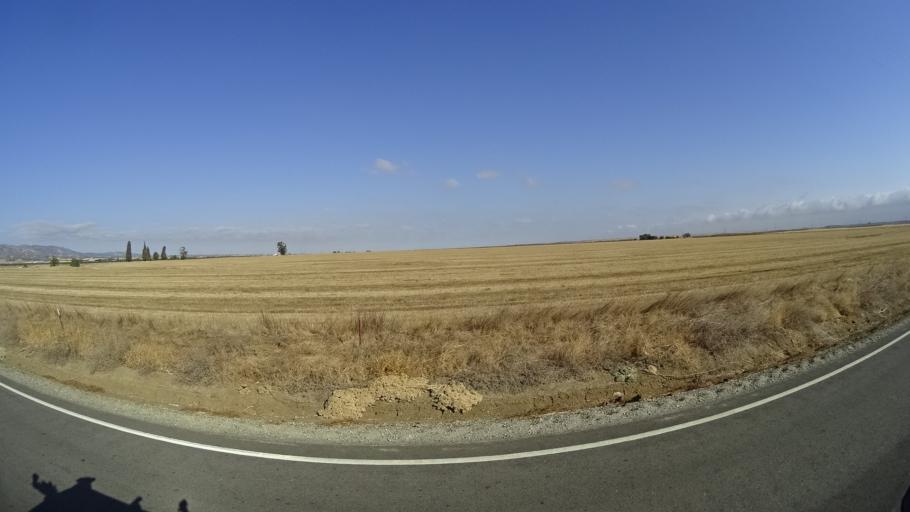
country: US
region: California
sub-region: Yolo County
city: Esparto
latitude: 38.7804
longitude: -122.0419
